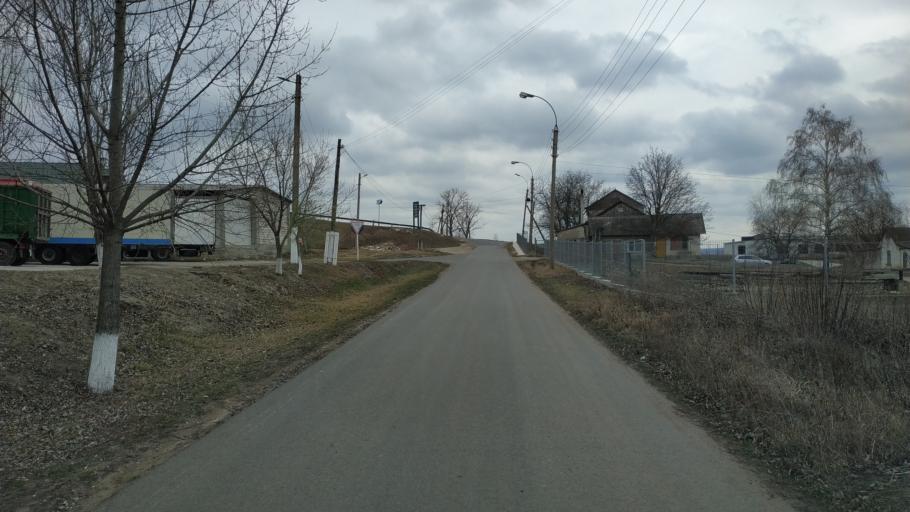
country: MD
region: Laloveni
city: Ialoveni
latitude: 46.8798
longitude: 28.7656
